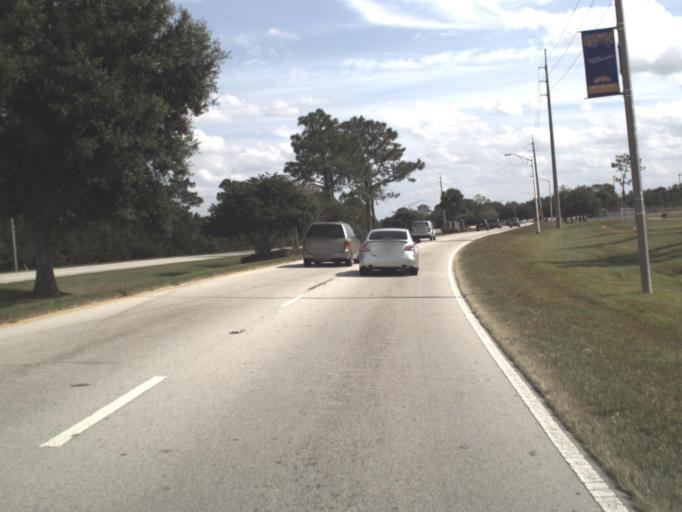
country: US
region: Florida
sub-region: Osceola County
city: Poinciana
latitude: 28.1462
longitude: -81.4618
